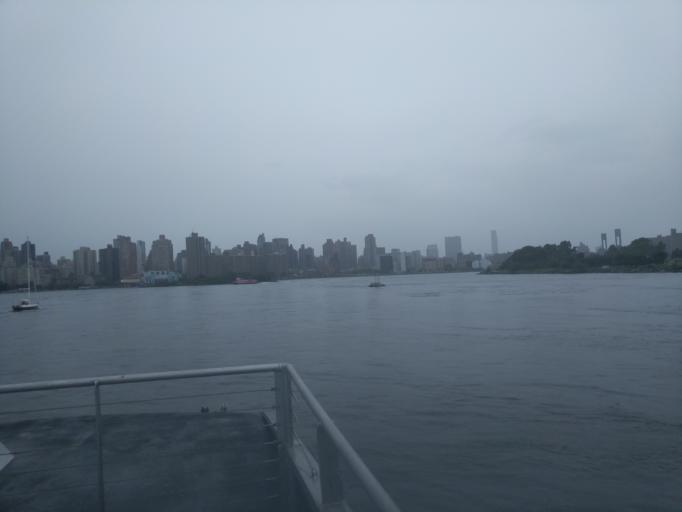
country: US
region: New York
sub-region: New York County
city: Manhattan
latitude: 40.7806
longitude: -73.9293
